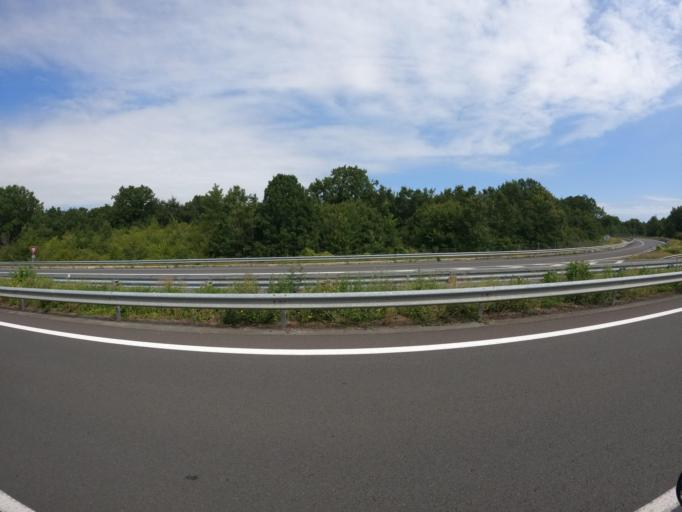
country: FR
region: Poitou-Charentes
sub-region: Departement de la Charente-Maritime
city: Courcon
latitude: 46.2218
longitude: -0.8128
